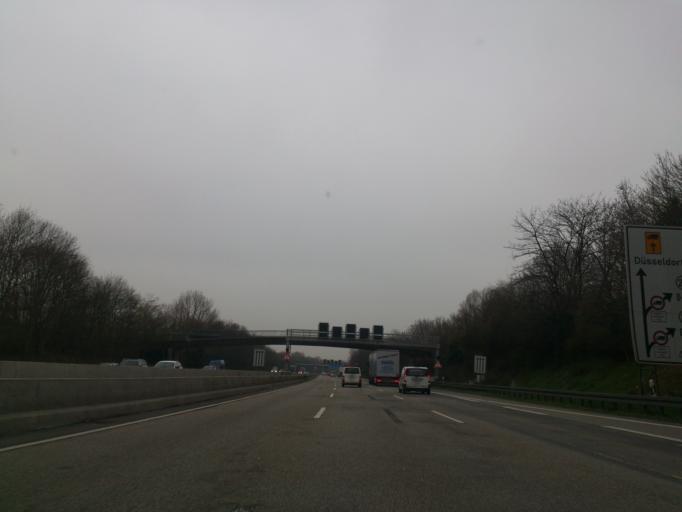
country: DE
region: North Rhine-Westphalia
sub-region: Regierungsbezirk Dusseldorf
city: Dusseldorf
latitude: 51.1902
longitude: 6.8373
